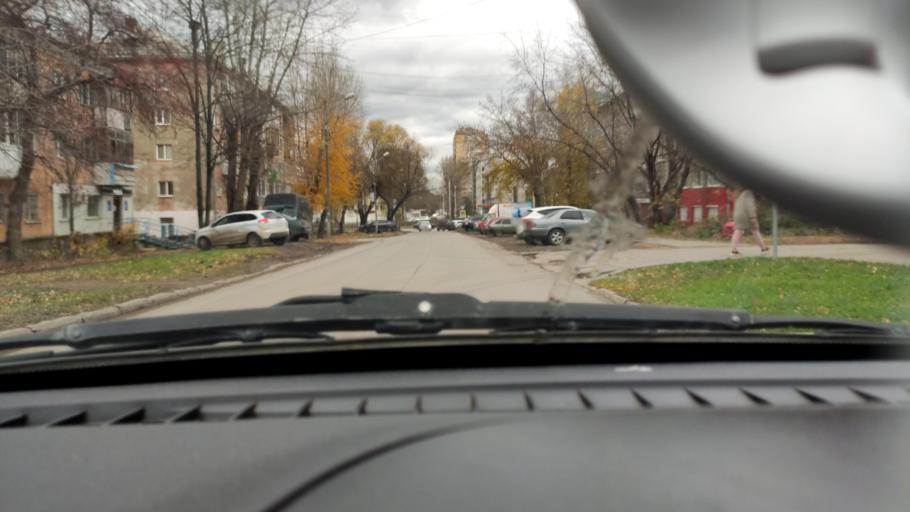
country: RU
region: Perm
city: Perm
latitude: 57.9851
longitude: 56.2136
